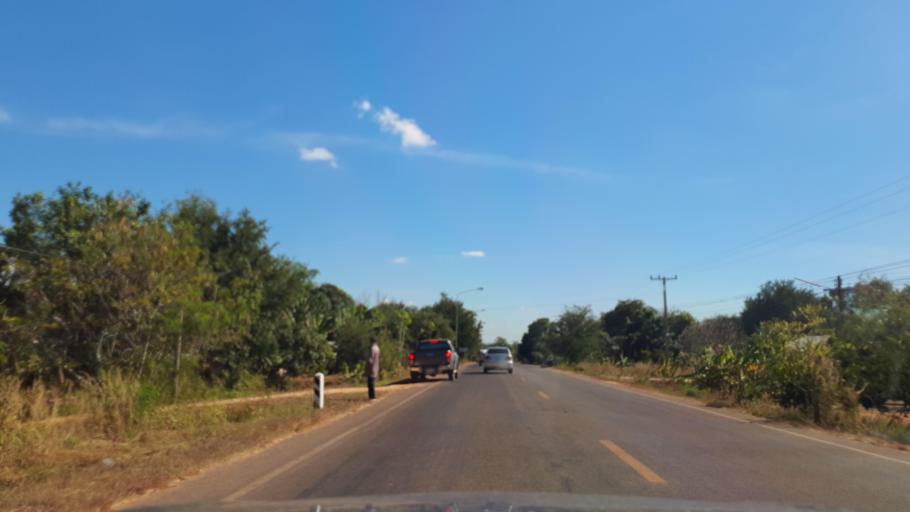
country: TH
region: Kalasin
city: Khao Wong
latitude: 16.7869
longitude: 104.1463
